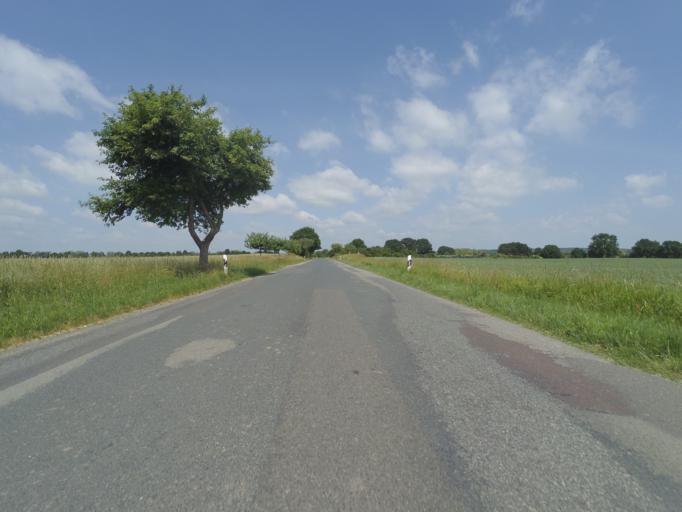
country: DE
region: Mecklenburg-Vorpommern
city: Lubz
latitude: 53.4470
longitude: 12.0133
